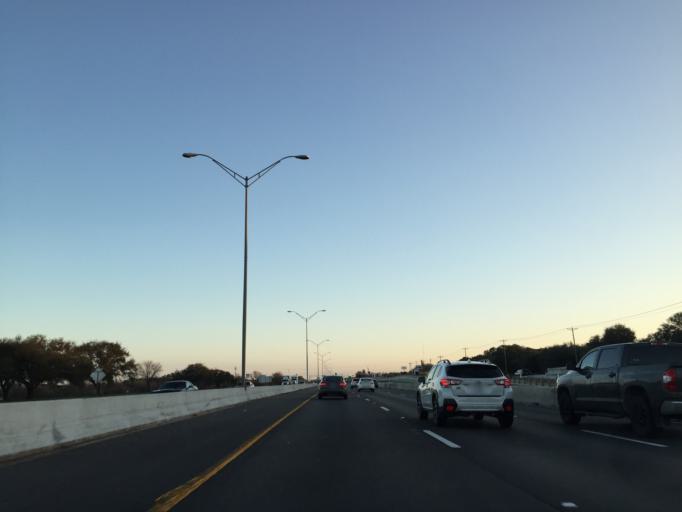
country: US
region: Texas
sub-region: Williamson County
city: Round Rock
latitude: 30.5511
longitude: -97.6925
